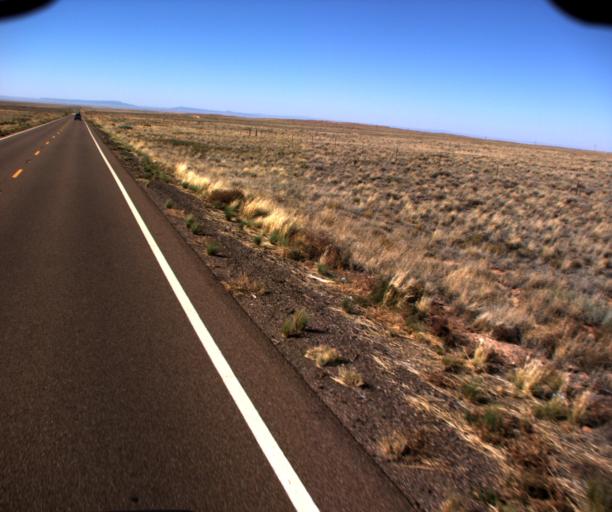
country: US
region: Arizona
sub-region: Navajo County
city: Joseph City
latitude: 35.1395
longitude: -110.4853
